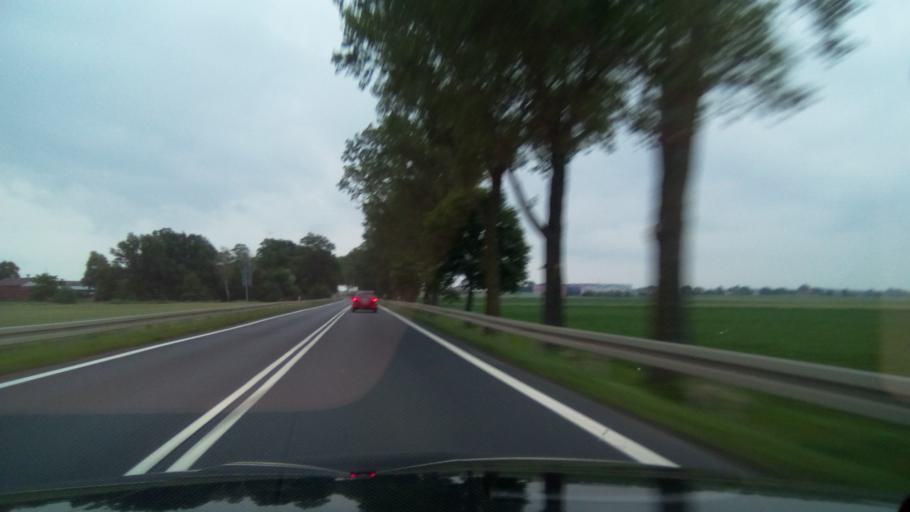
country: PL
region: Greater Poland Voivodeship
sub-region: Powiat poznanski
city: Pobiedziska
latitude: 52.4901
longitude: 17.3178
